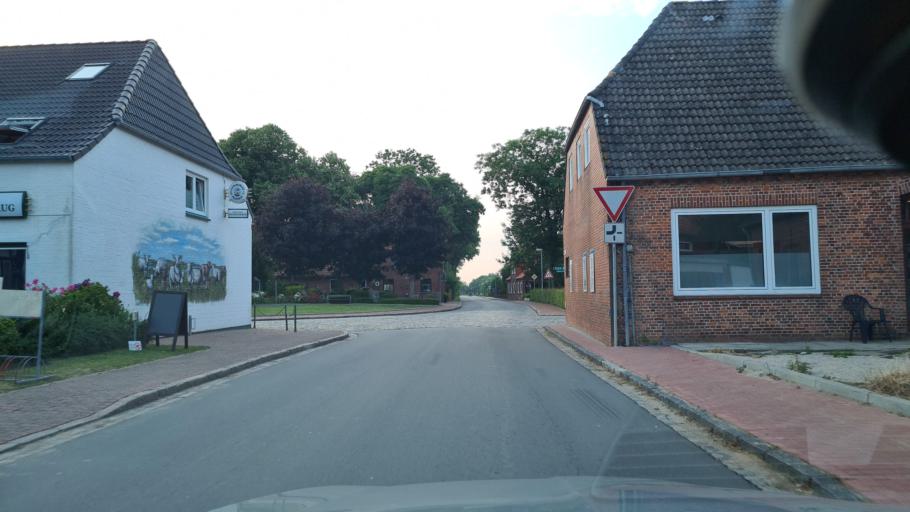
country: DE
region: Schleswig-Holstein
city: Oldenswort
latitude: 54.3726
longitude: 8.9428
